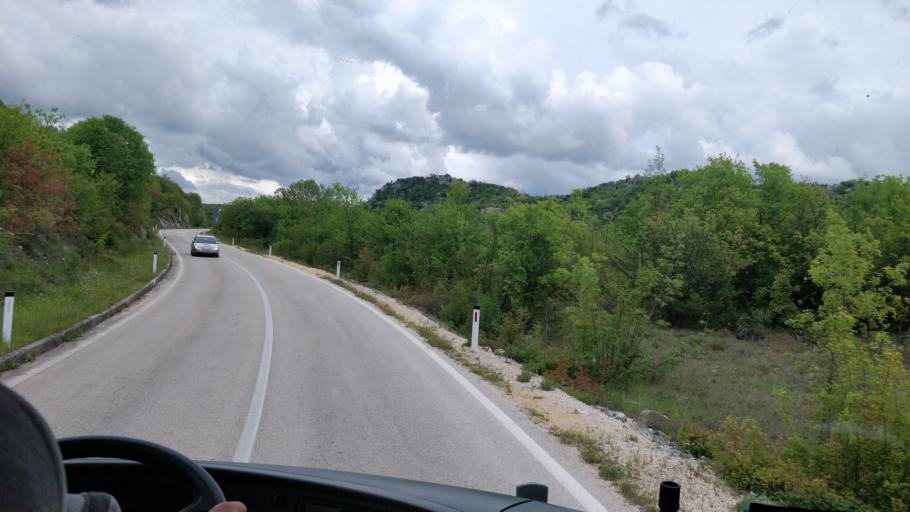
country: BA
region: Federation of Bosnia and Herzegovina
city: Ljubuski
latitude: 43.1740
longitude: 17.4902
